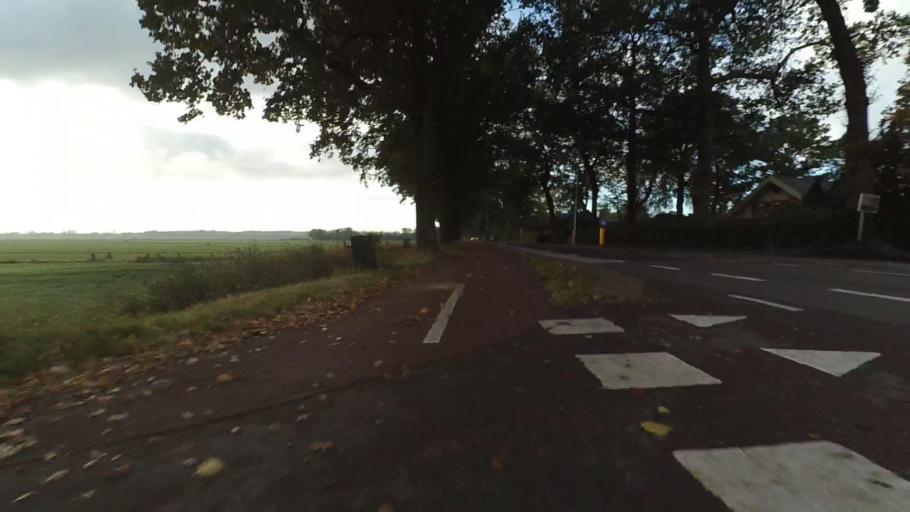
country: NL
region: Utrecht
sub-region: Gemeente Baarn
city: Baarn
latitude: 52.2369
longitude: 5.2608
